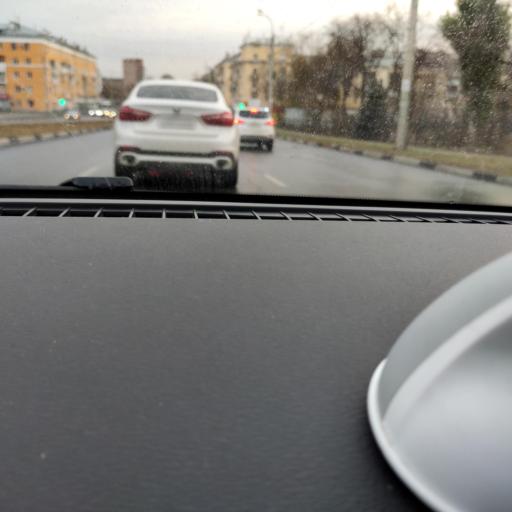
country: RU
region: Samara
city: Samara
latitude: 53.2015
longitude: 50.2193
